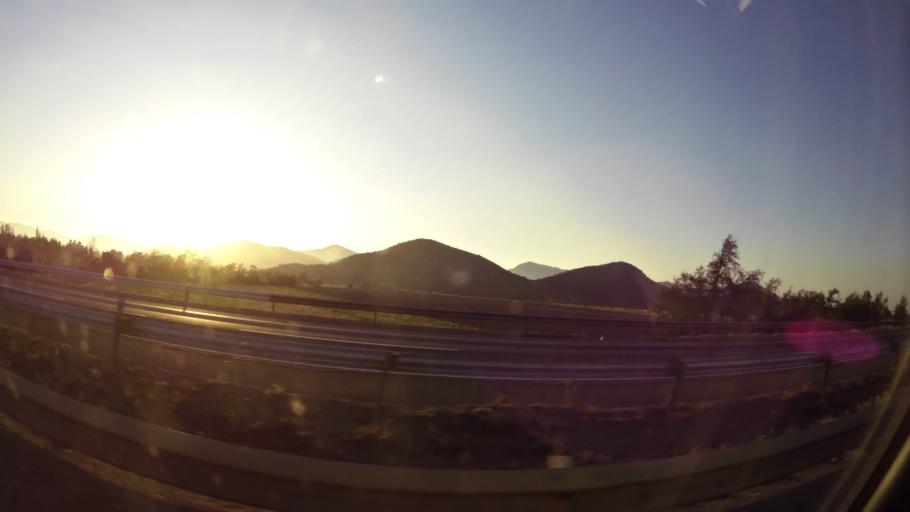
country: CL
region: Santiago Metropolitan
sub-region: Provincia de Talagante
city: Penaflor
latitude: -33.5449
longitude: -70.8055
